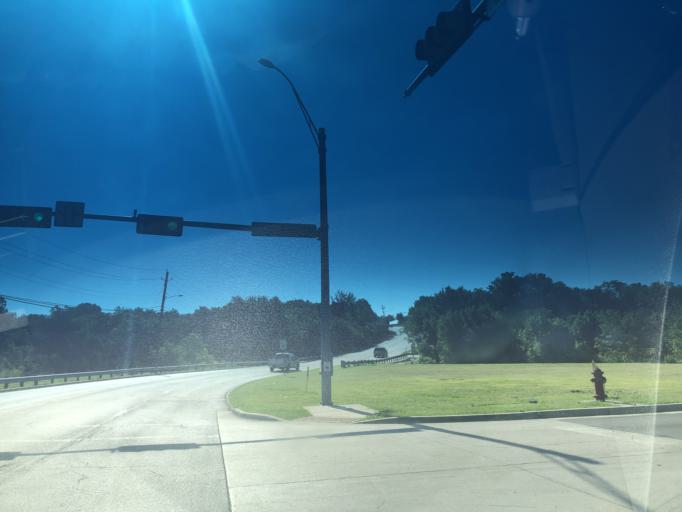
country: US
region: Texas
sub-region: Dallas County
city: Grand Prairie
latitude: 32.7210
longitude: -97.0197
